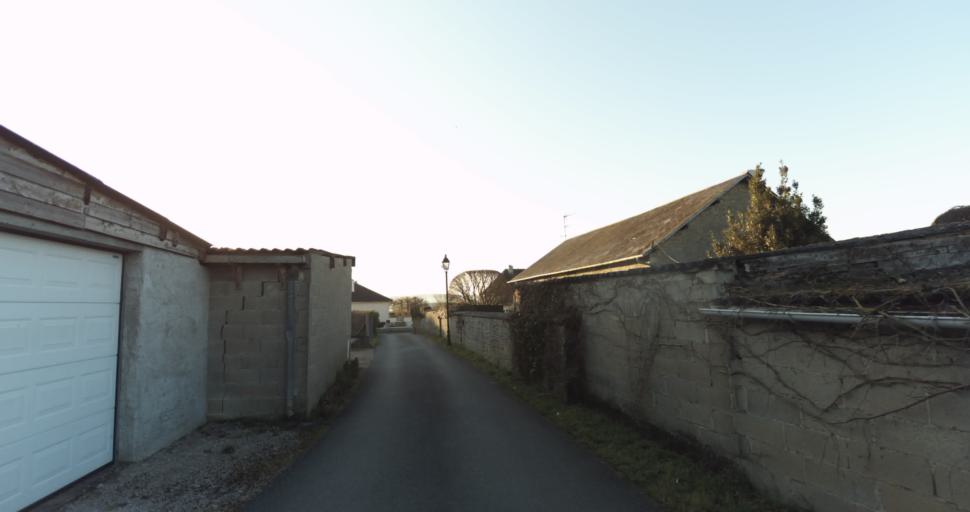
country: FR
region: Lower Normandy
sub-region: Departement du Calvados
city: Saint-Pierre-sur-Dives
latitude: 49.0342
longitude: -0.0285
